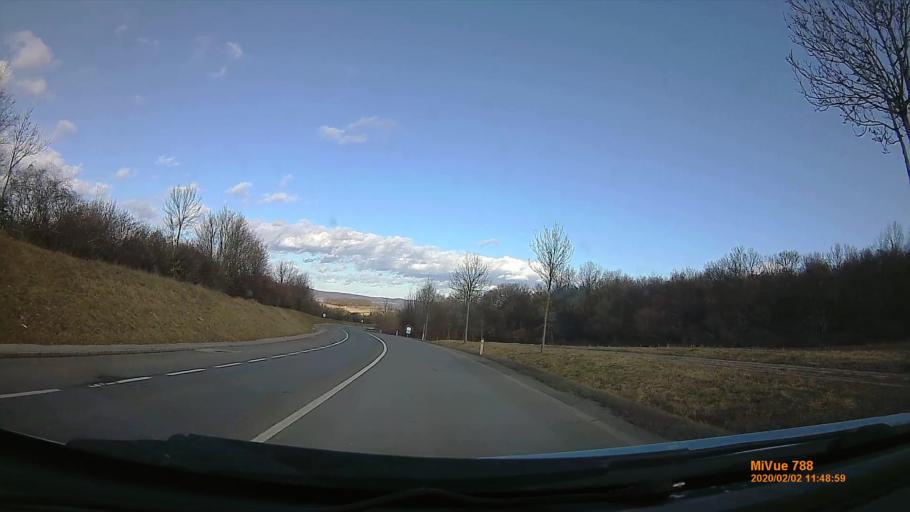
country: AT
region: Burgenland
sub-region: Eisenstadt-Umgebung
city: Klingenbach
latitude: 47.7475
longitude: 16.5452
